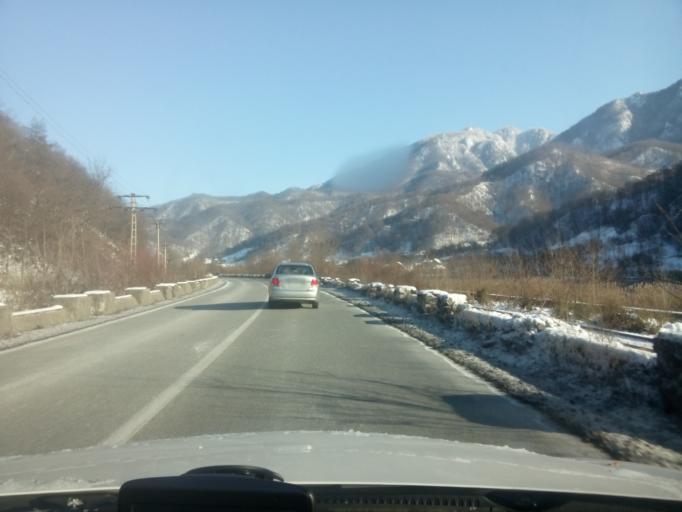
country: RO
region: Valcea
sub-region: Comuna Brezoi
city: Brezoi
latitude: 45.3509
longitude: 24.2898
